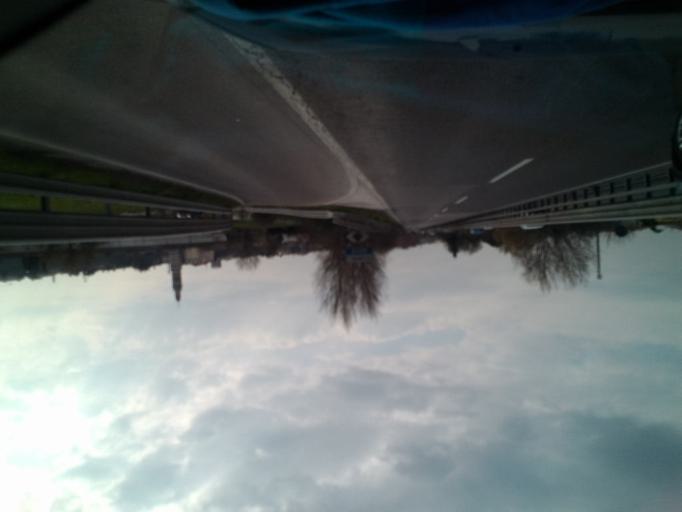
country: IT
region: Veneto
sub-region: Provincia di Verona
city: Pescantina
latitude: 45.4844
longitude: 10.8589
